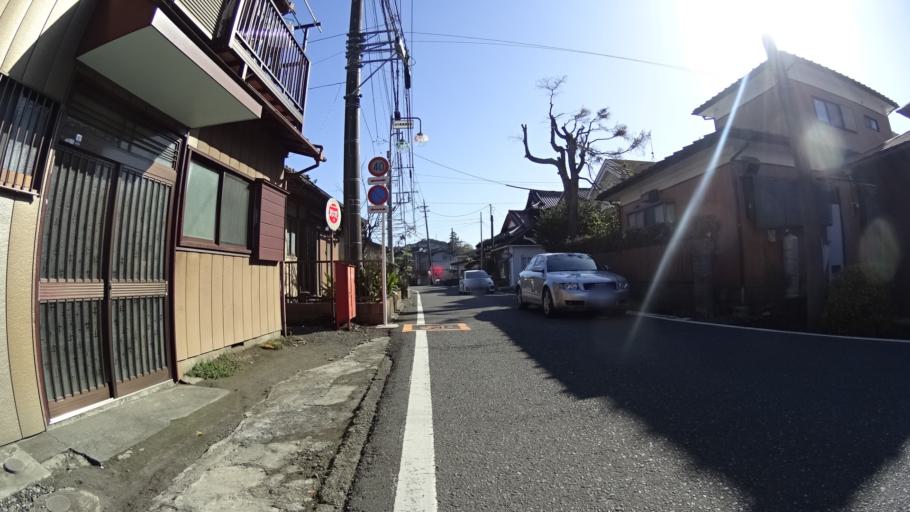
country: JP
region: Kanagawa
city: Zama
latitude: 35.5286
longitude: 139.2869
